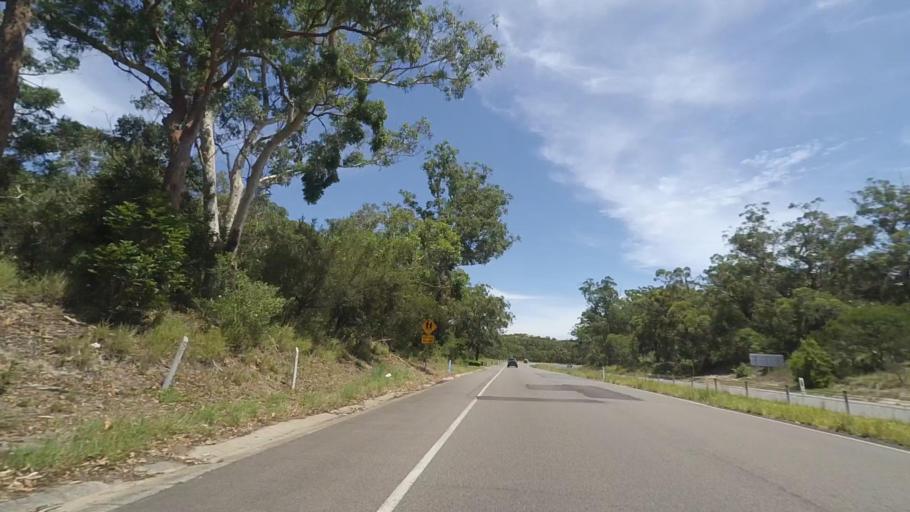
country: AU
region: New South Wales
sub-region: Port Stephens Shire
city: Anna Bay
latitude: -32.7698
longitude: 152.0119
